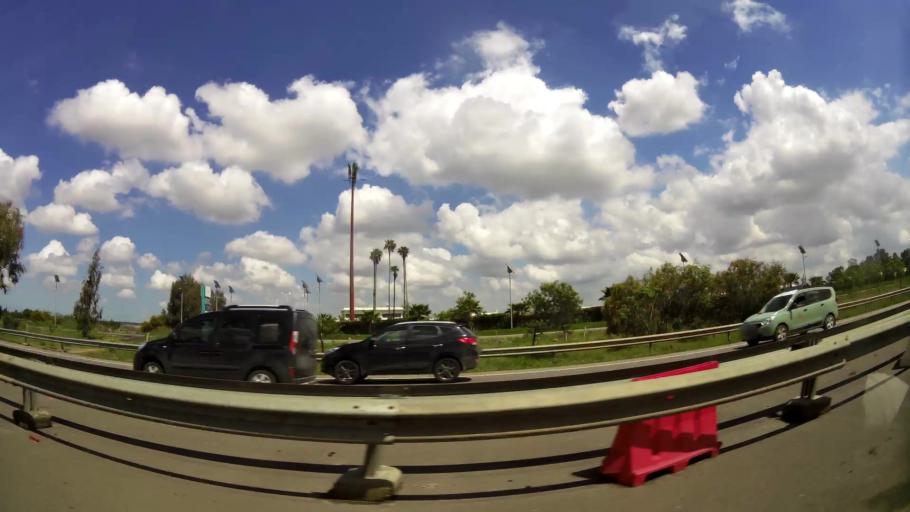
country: MA
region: Chaouia-Ouardigha
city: Nouaseur
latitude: 33.4059
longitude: -7.6243
